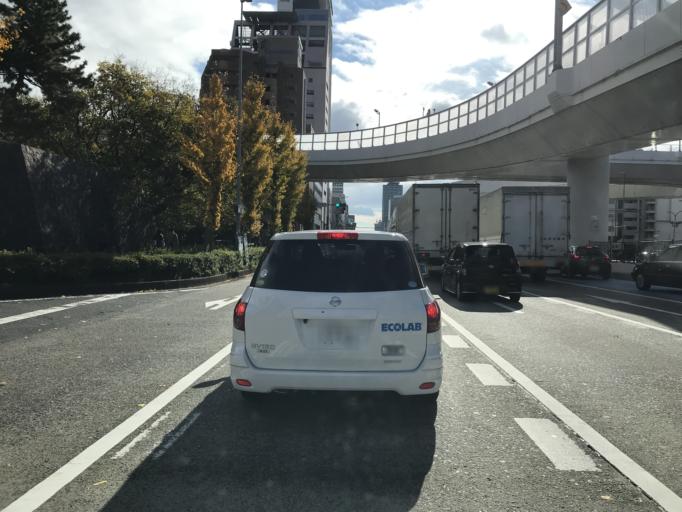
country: JP
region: Aichi
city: Nagoya-shi
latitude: 35.1784
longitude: 136.8966
